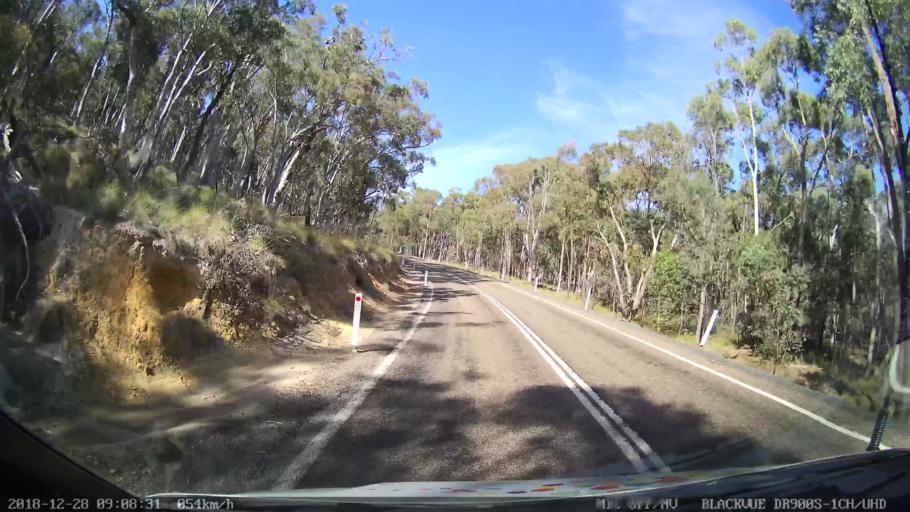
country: AU
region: New South Wales
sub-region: Upper Lachlan Shire
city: Crookwell
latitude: -34.2133
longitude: 149.3384
